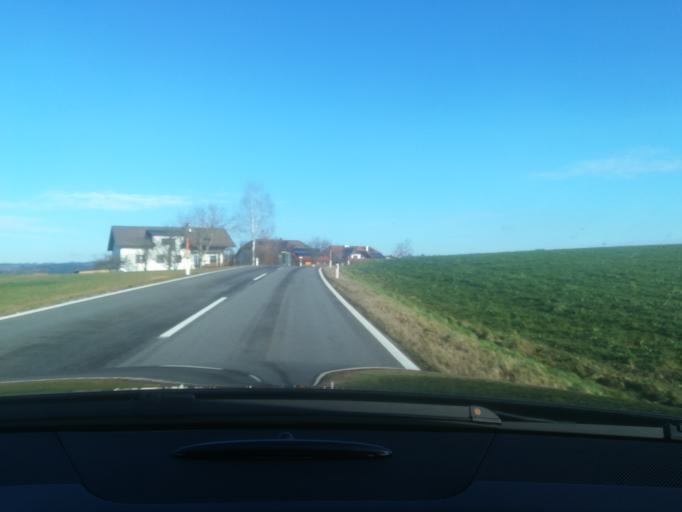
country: AT
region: Upper Austria
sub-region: Politischer Bezirk Urfahr-Umgebung
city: Herzogsdorf
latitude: 48.4181
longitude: 14.0939
